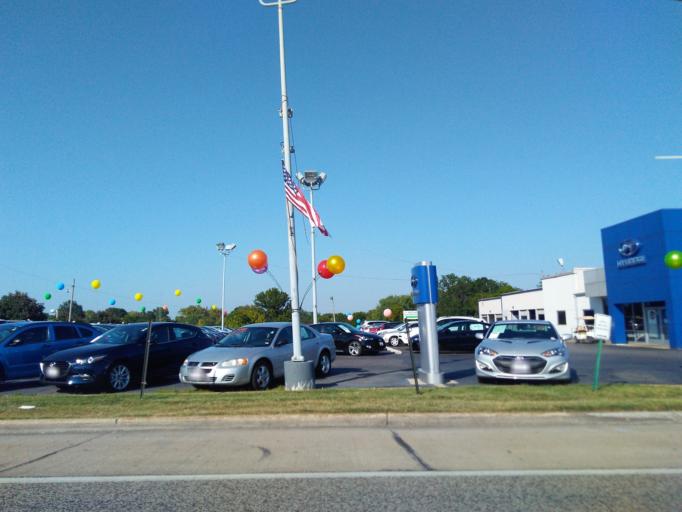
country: US
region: Missouri
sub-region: Saint Louis County
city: Green Park
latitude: 38.5212
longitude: -90.3459
